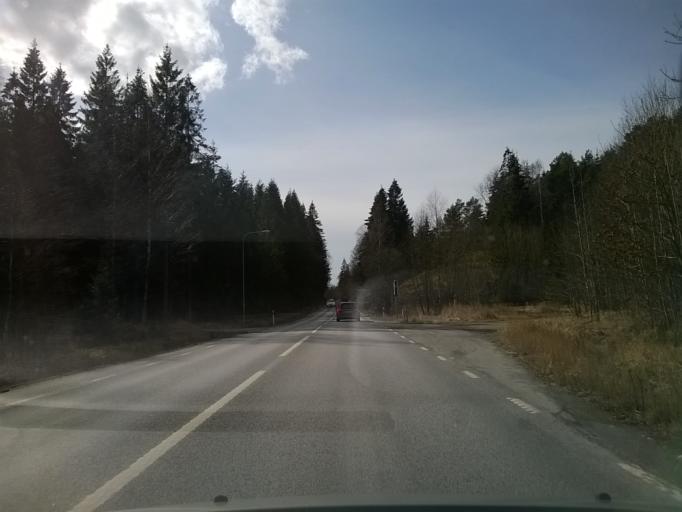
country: SE
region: Vaestra Goetaland
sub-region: Tjorns Kommun
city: Myggenas
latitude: 58.1212
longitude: 11.7158
